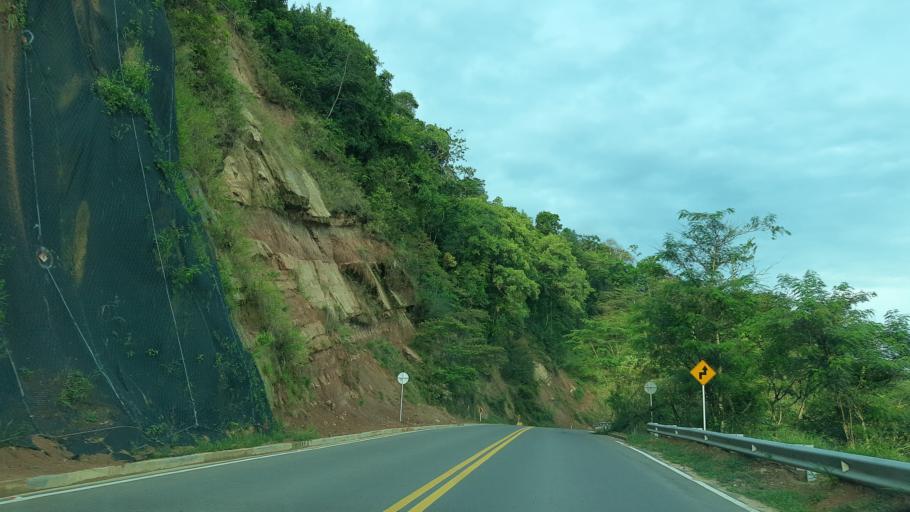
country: CO
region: Boyaca
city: San Luis de Gaceno
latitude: 4.8312
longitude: -73.1194
